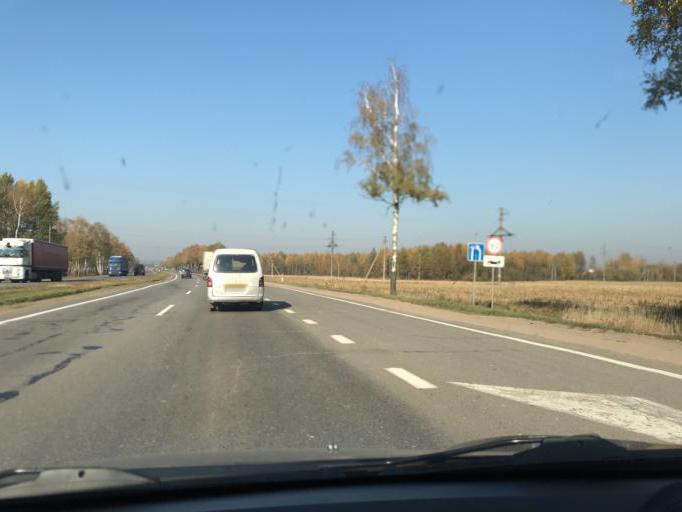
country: BY
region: Minsk
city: Luhavaya Slabada
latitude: 53.7755
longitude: 27.8270
